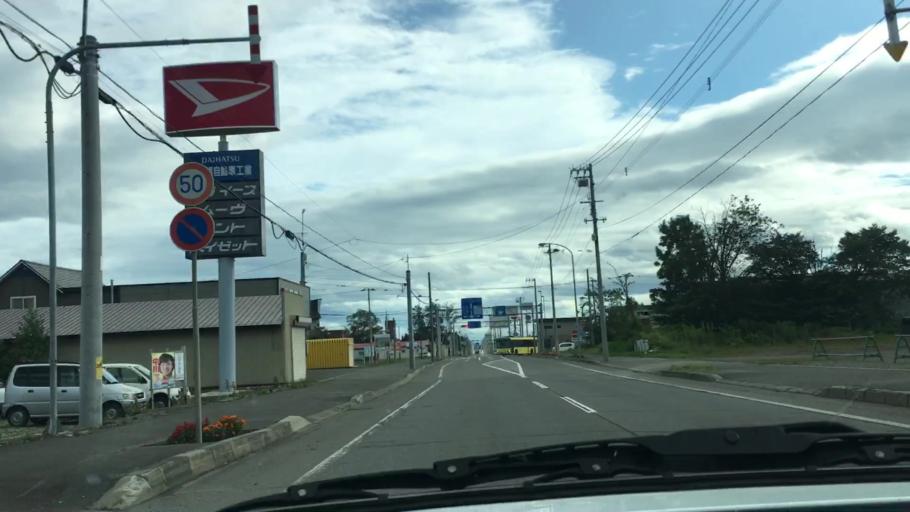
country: JP
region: Hokkaido
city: Otofuke
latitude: 43.2359
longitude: 143.2958
